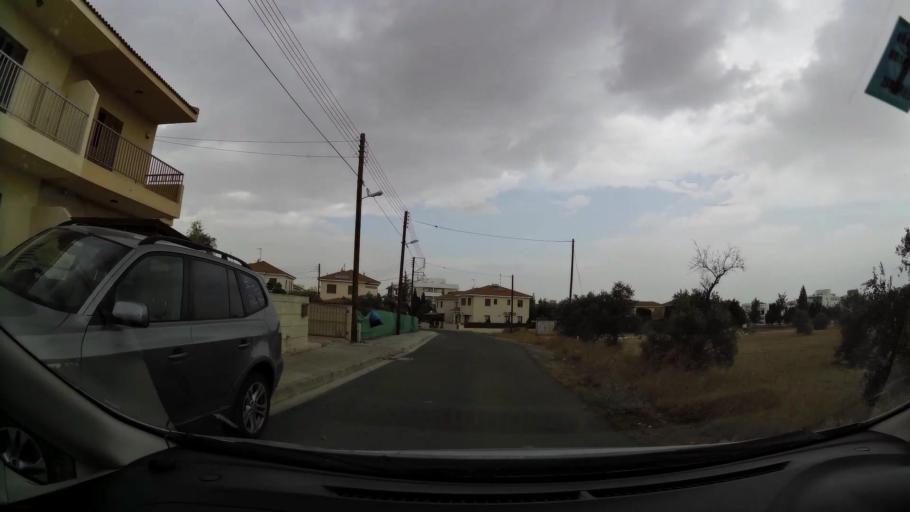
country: CY
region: Lefkosia
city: Geri
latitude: 35.0977
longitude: 33.3843
